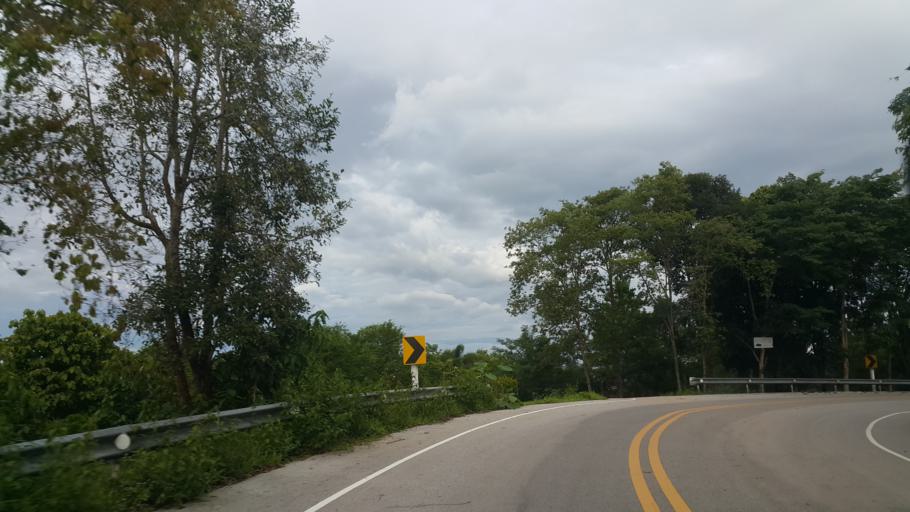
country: TH
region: Loei
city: Na Haeo
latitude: 17.5037
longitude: 101.0899
